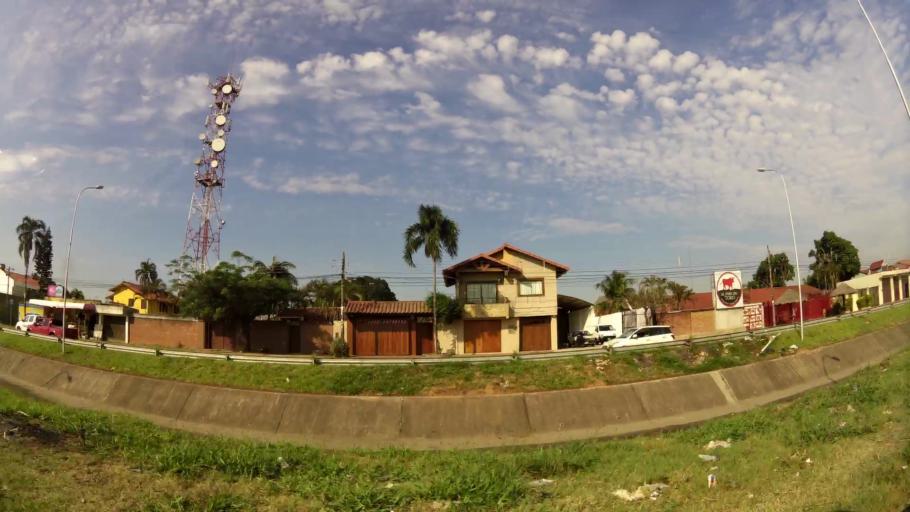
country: BO
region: Santa Cruz
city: Santa Cruz de la Sierra
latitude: -17.7364
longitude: -63.1565
